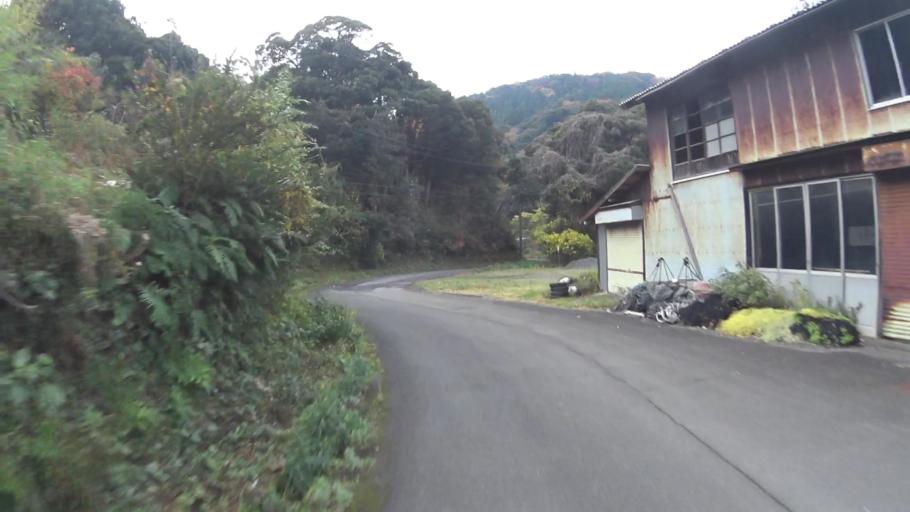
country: JP
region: Kyoto
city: Maizuru
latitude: 35.5601
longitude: 135.4652
